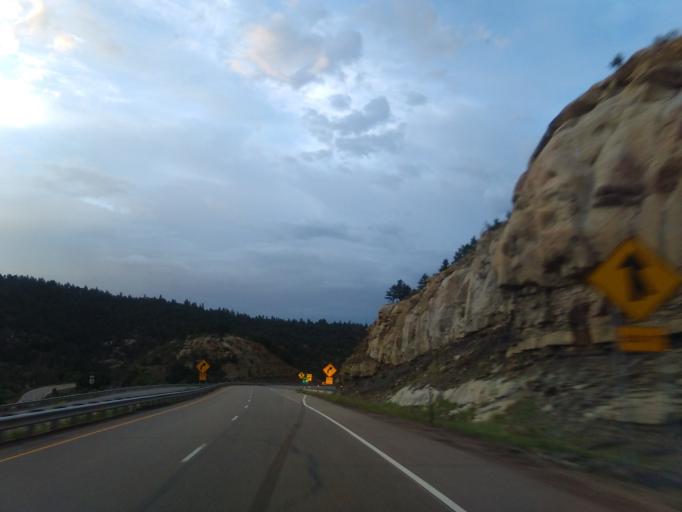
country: US
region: Colorado
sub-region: Las Animas County
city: Trinidad
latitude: 37.0582
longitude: -104.5228
